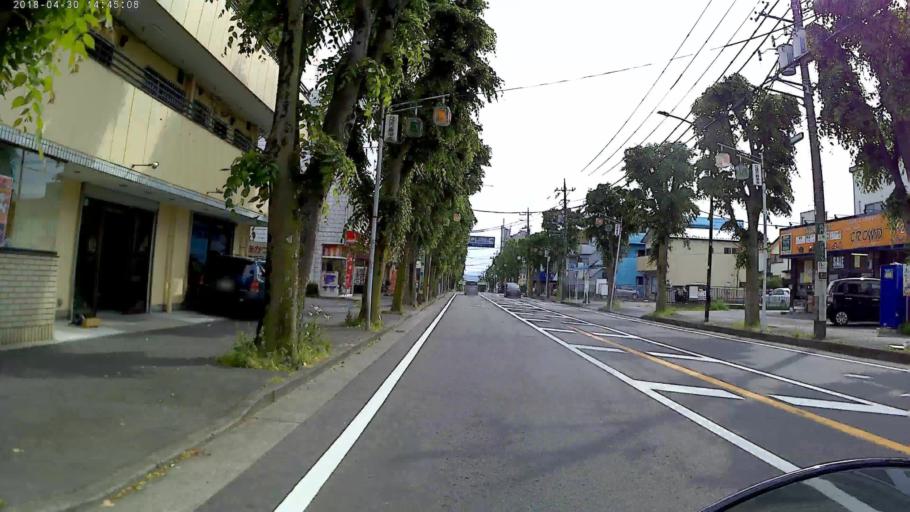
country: JP
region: Kanagawa
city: Zama
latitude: 35.5634
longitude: 139.3685
